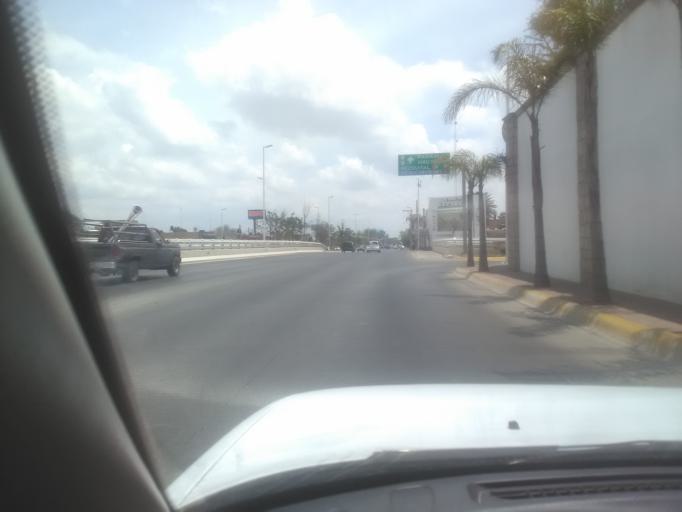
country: MX
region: Durango
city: Victoria de Durango
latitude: 24.0358
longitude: -104.6807
